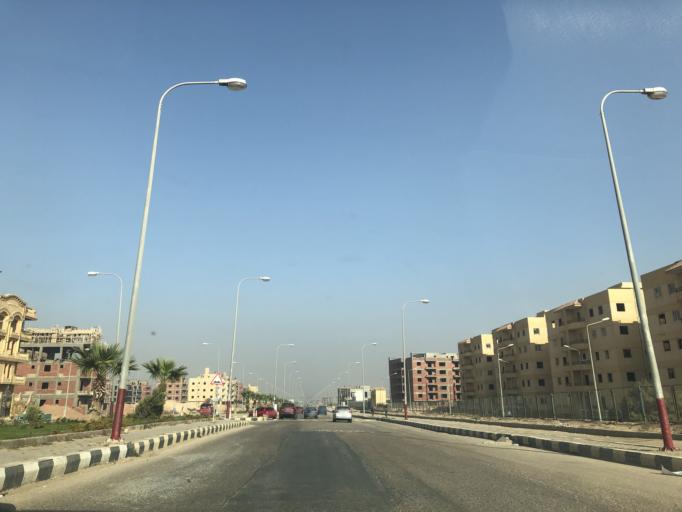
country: EG
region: Al Jizah
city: Madinat Sittah Uktubar
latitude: 29.9366
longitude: 31.0494
